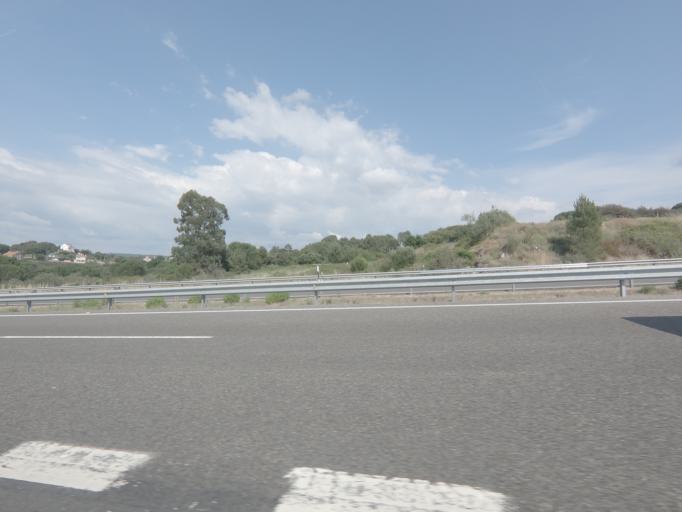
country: ES
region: Galicia
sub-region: Provincia de Ourense
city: Ourense
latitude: 42.3018
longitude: -7.8756
